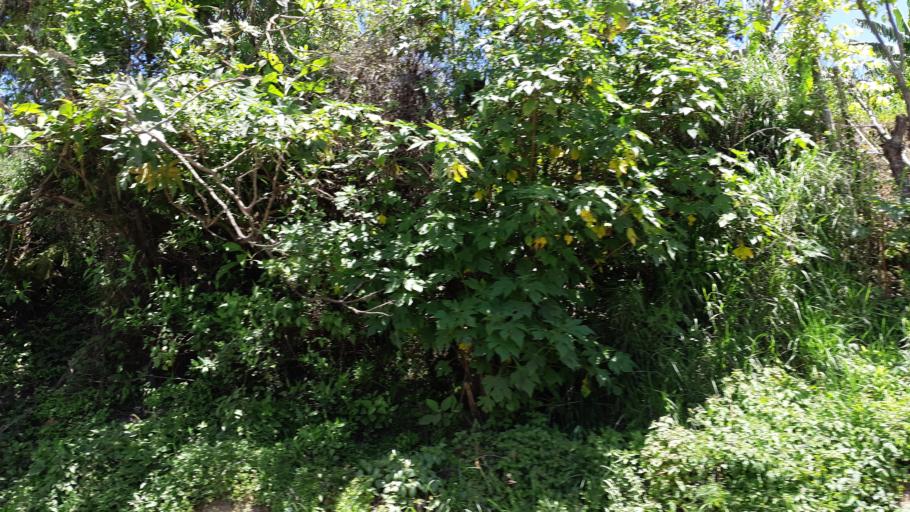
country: GT
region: Chimaltenango
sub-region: Municipio de Zaragoza
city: Zaragoza
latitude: 14.6538
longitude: -90.8607
